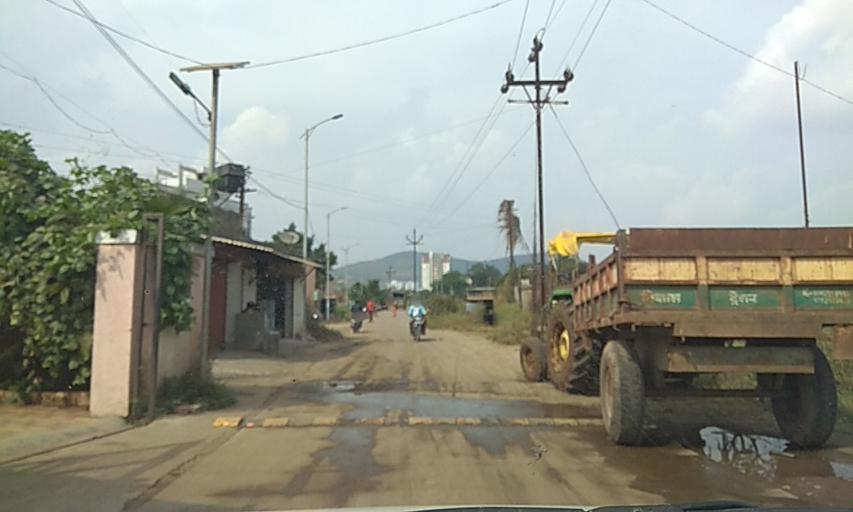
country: IN
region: Maharashtra
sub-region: Pune Division
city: Pimpri
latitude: 18.5827
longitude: 73.7064
